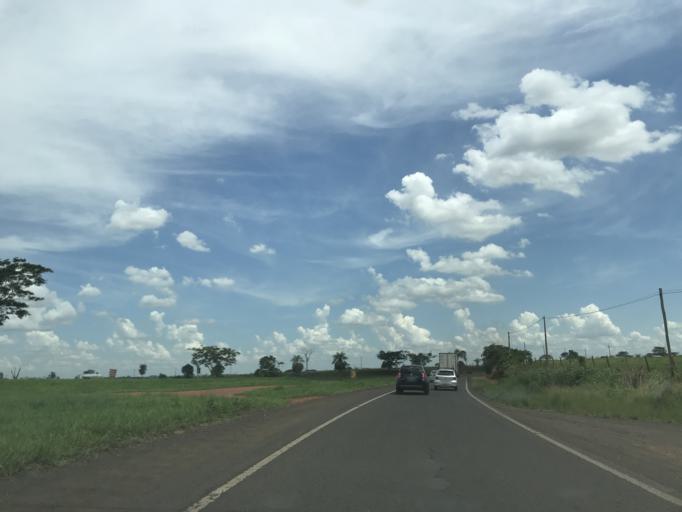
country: BR
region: Sao Paulo
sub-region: Nova Granada
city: Nova Granada
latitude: -20.3245
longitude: -49.2131
